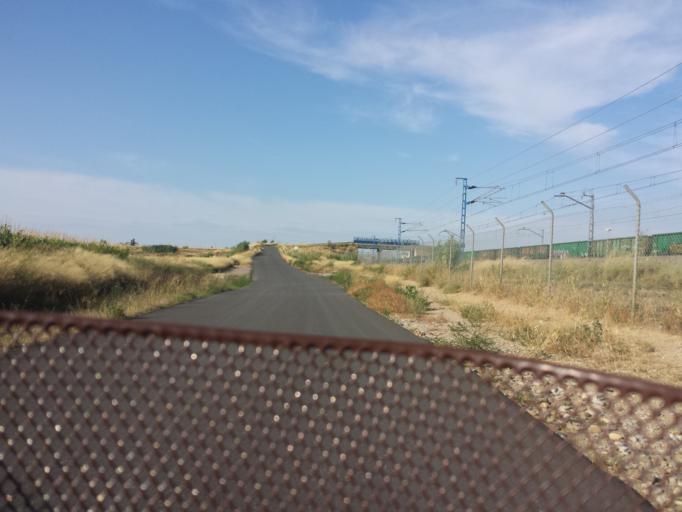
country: ES
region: Aragon
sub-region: Provincia de Zaragoza
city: Zaragoza
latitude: 41.7048
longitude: -0.8518
